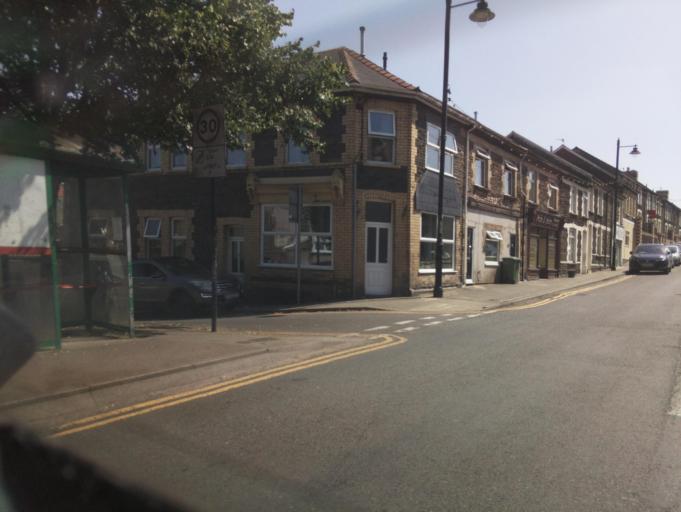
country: GB
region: Wales
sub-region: Caerphilly County Borough
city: Llanbradach
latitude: 51.6035
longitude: -3.2312
